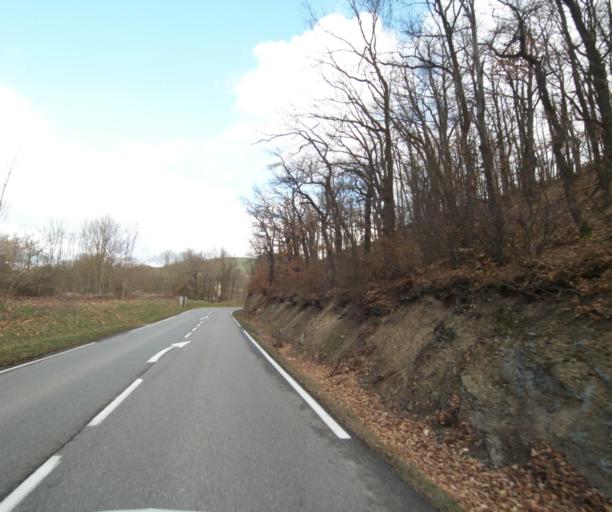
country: FR
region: Rhone-Alpes
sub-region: Departement de la Loire
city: La Talaudiere
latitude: 45.4741
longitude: 4.4119
